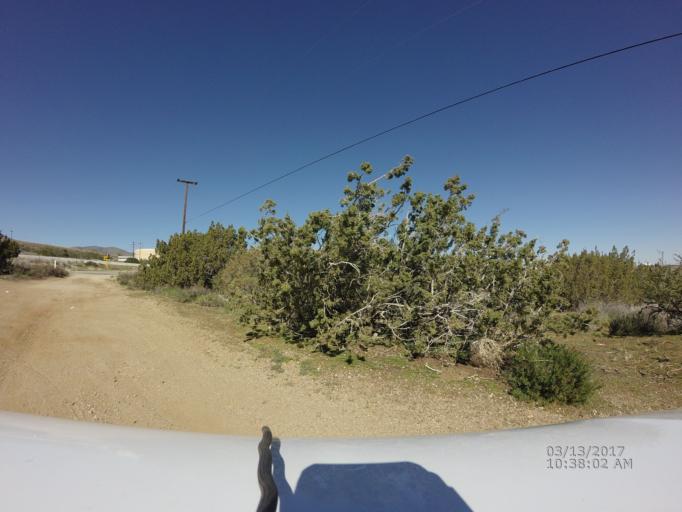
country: US
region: California
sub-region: Los Angeles County
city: Palmdale
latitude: 34.5494
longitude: -118.1305
